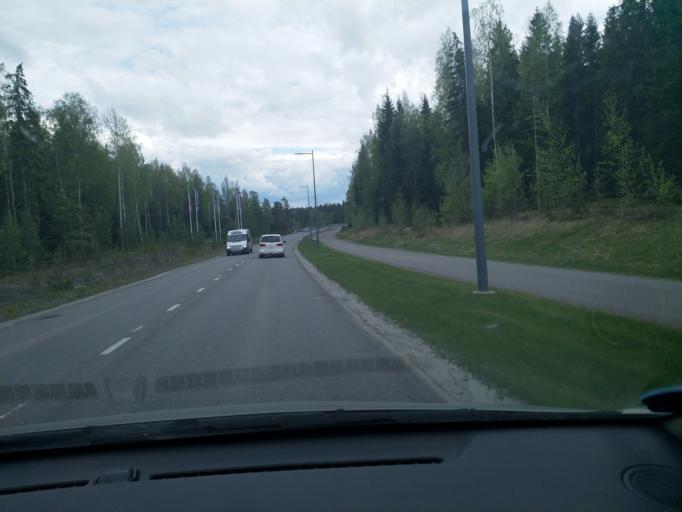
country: FI
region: Pirkanmaa
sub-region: Tampere
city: Tampere
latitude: 61.4517
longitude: 23.8021
